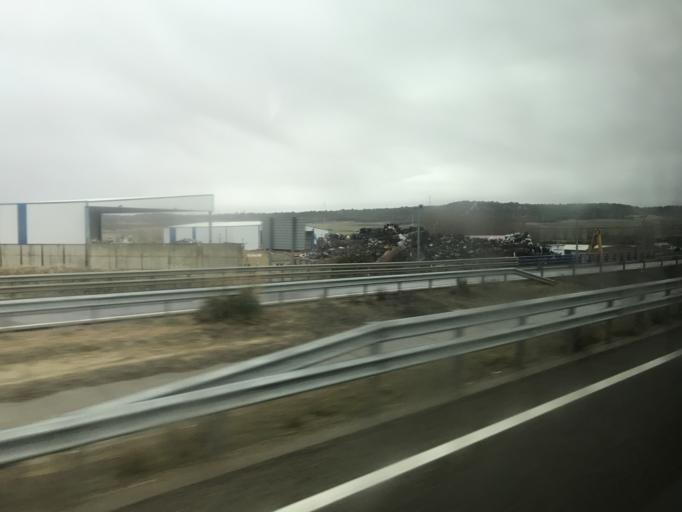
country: ES
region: Castille and Leon
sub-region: Provincia de Palencia
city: Villalobon
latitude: 42.0223
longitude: -4.5128
